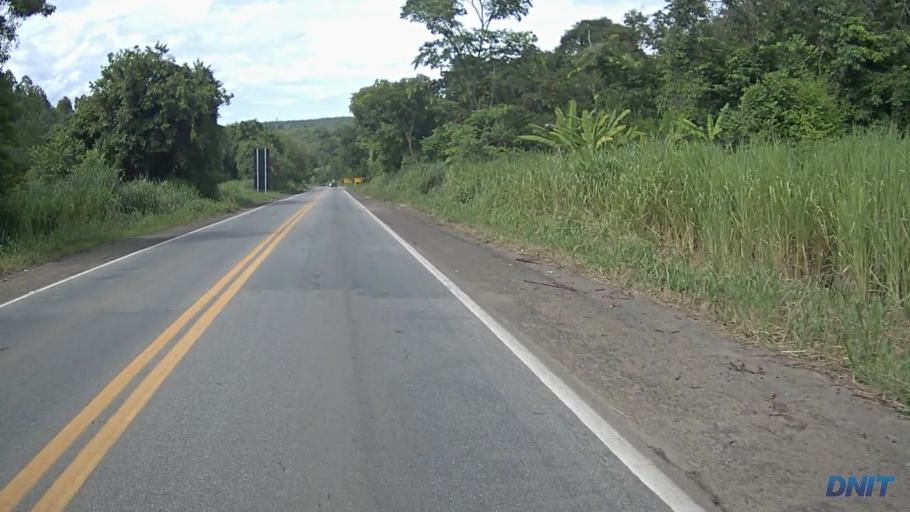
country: BR
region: Minas Gerais
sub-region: Ipaba
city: Ipaba
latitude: -19.3401
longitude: -42.4288
